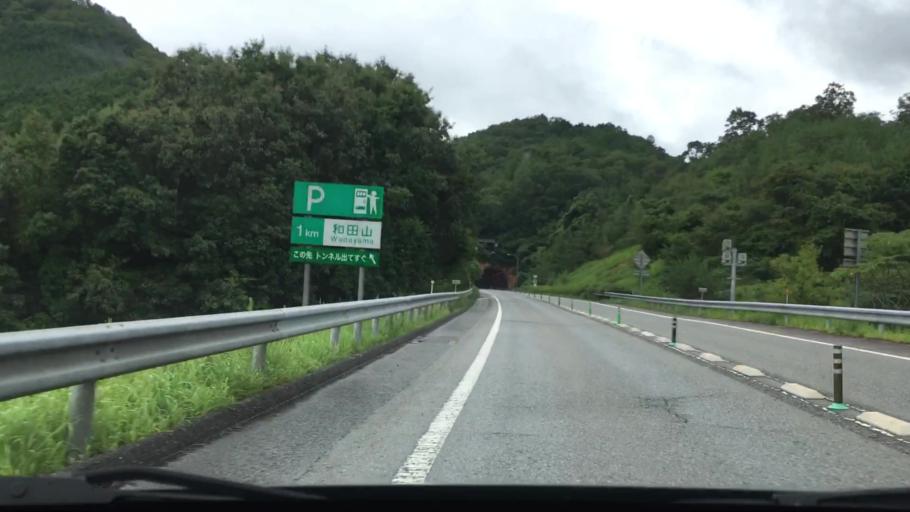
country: JP
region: Hyogo
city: Toyooka
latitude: 35.3060
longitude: 134.8254
